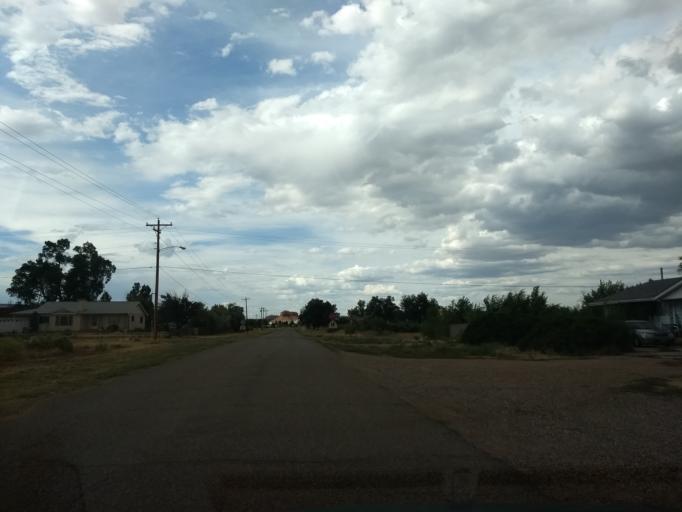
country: US
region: Arizona
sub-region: Coconino County
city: Fredonia
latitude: 36.9520
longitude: -112.5243
